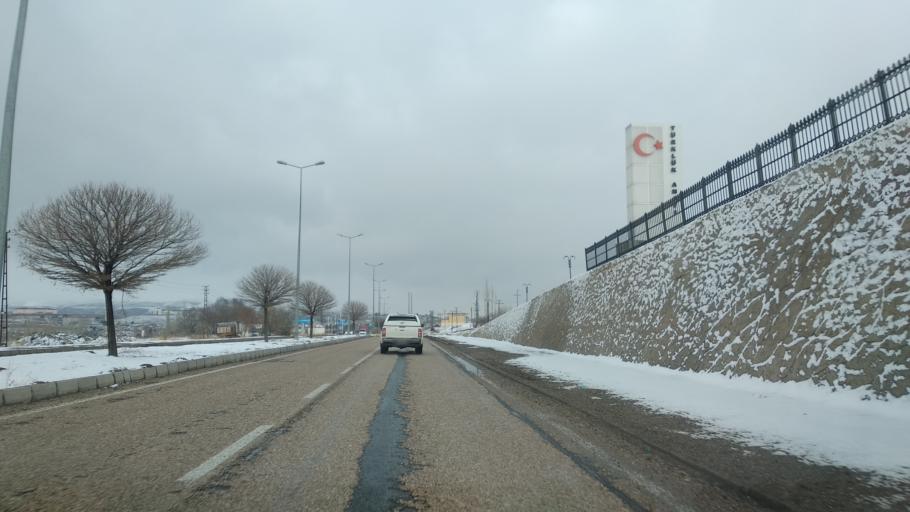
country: TR
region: Kayseri
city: Pinarbasi
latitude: 38.7120
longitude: 36.3786
